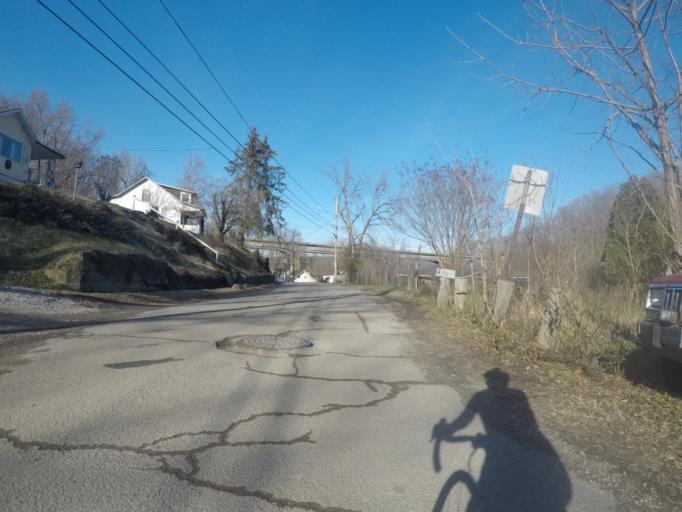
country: US
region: West Virginia
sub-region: Cabell County
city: Huntington
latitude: 38.3985
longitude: -82.4873
